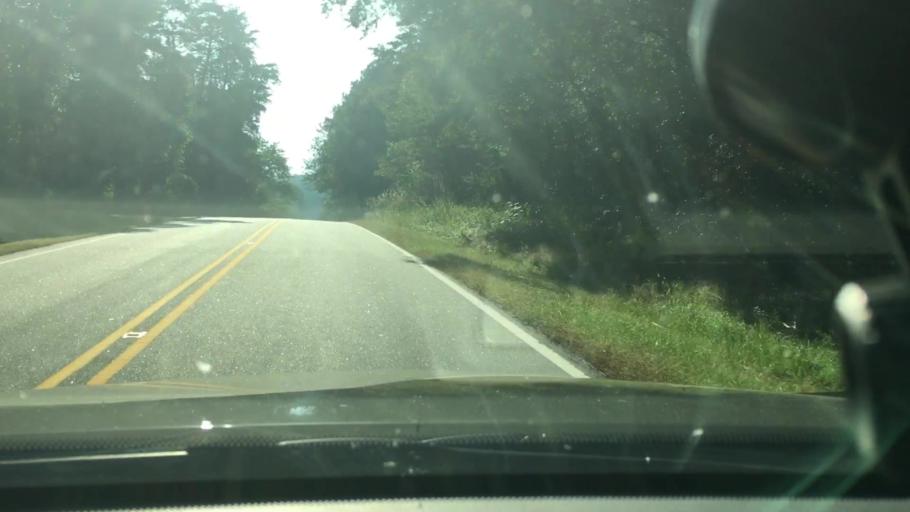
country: US
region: North Carolina
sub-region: Rutherford County
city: Rutherfordton
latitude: 35.3548
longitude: -81.9908
